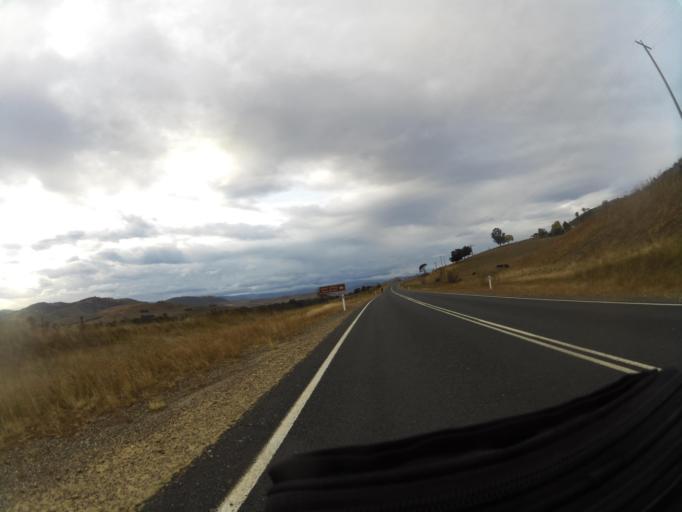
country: AU
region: New South Wales
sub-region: Snowy River
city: Jindabyne
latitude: -36.0816
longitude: 147.9762
